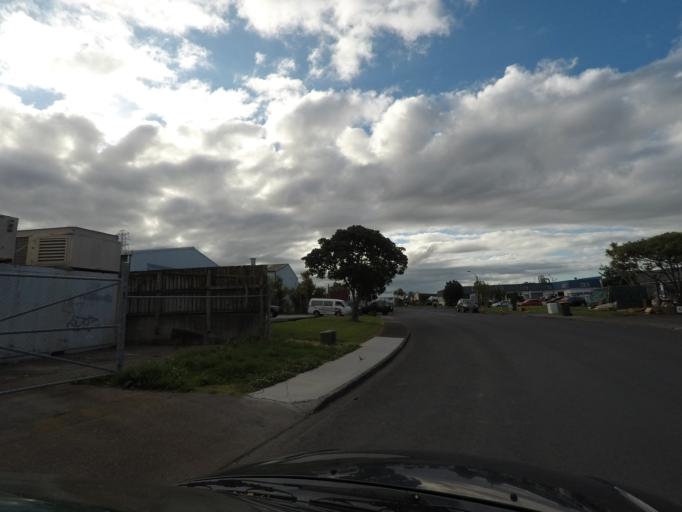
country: NZ
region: Auckland
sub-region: Auckland
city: Rosebank
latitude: -36.8870
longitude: 174.6640
